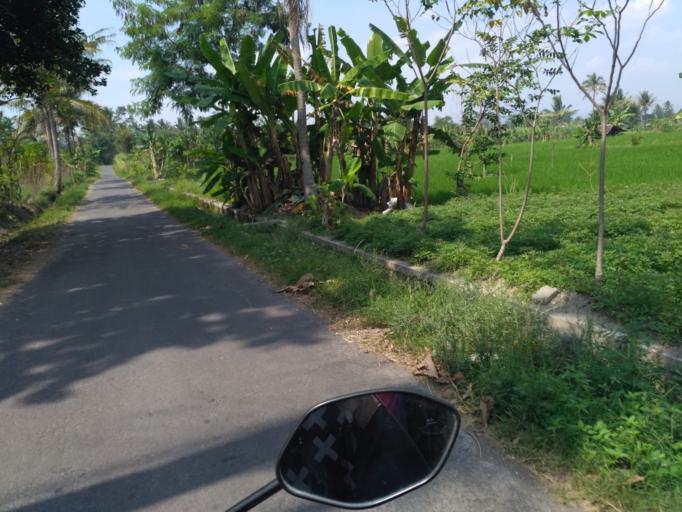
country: ID
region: Daerah Istimewa Yogyakarta
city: Depok
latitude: -7.7107
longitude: 110.4208
